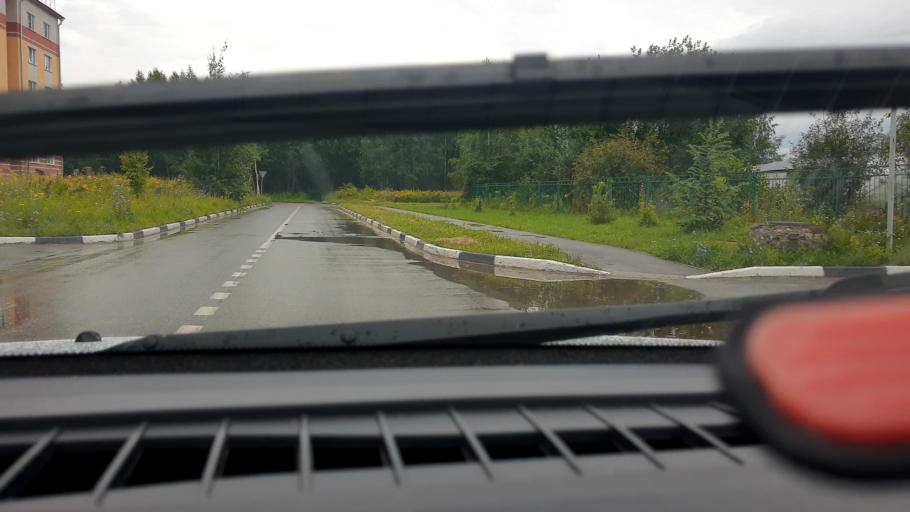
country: RU
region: Nizjnij Novgorod
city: Neklyudovo
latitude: 56.3824
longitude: 44.0198
